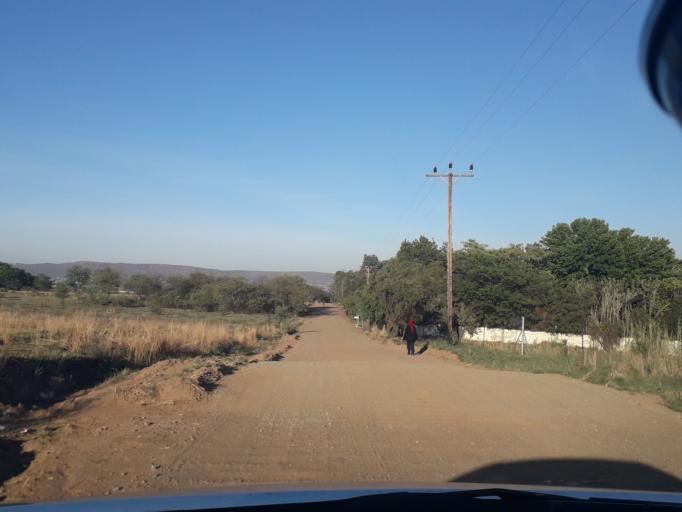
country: ZA
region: Gauteng
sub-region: West Rand District Municipality
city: Muldersdriseloop
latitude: -26.0524
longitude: 27.8879
